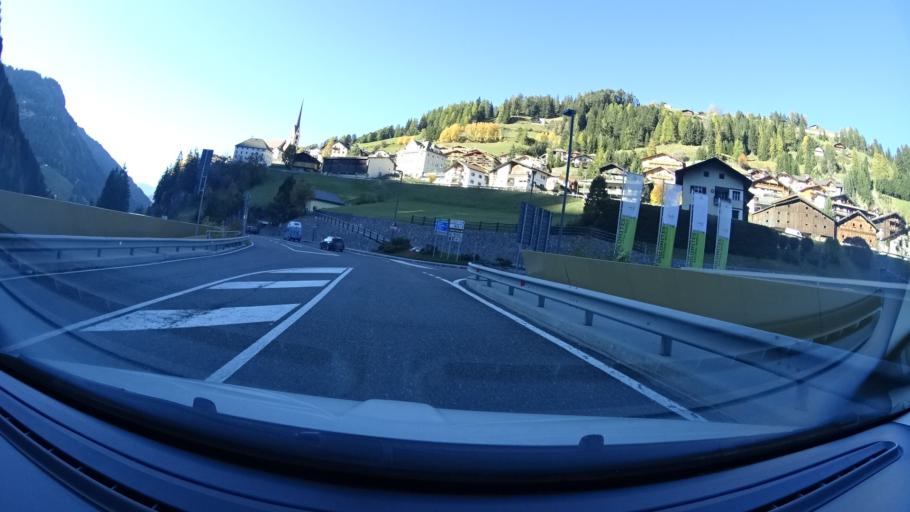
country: IT
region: Trentino-Alto Adige
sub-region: Bolzano
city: Santa Cristina Valgardena
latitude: 46.5575
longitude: 11.7186
